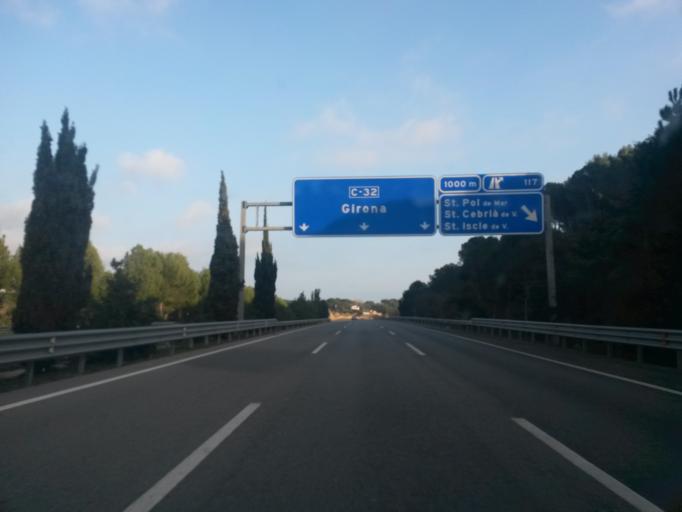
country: ES
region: Catalonia
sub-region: Provincia de Barcelona
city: Canet de Mar
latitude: 41.6009
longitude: 2.5933
